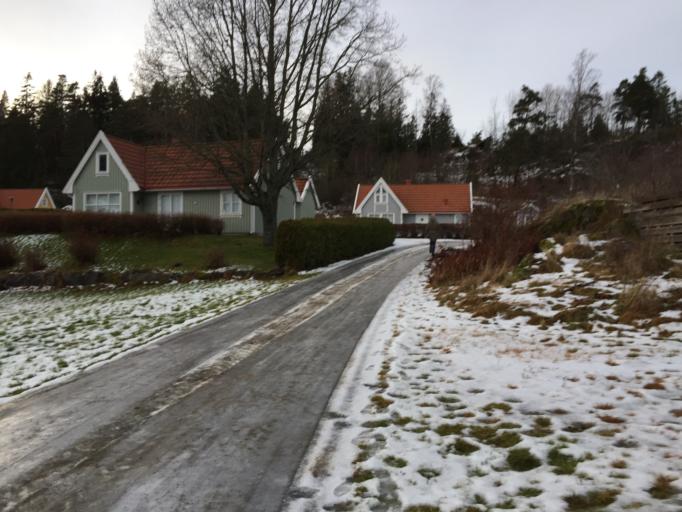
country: NO
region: Ostfold
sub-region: Moss
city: Moss
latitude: 59.4861
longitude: 10.6735
